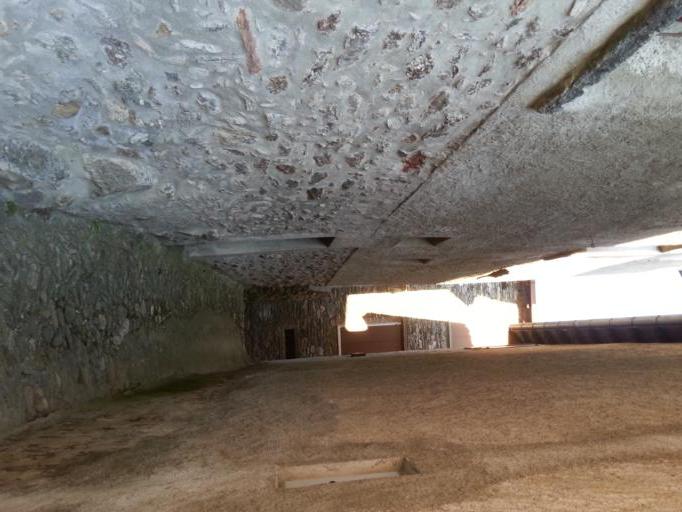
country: IT
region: Lombardy
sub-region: Provincia di Como
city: Plesio
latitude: 46.0594
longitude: 9.2475
